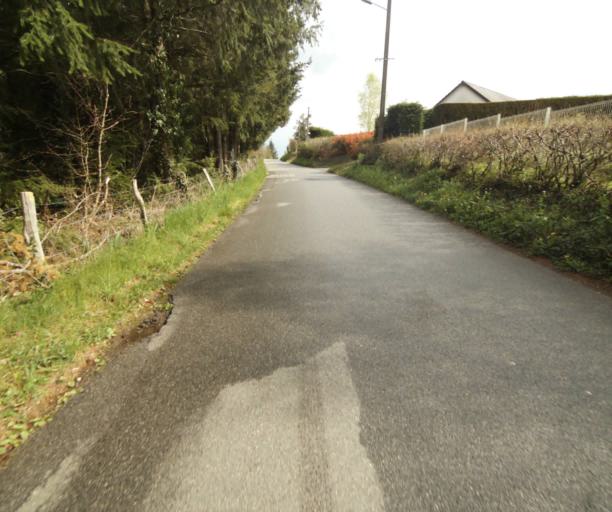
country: FR
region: Limousin
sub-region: Departement de la Correze
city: Tulle
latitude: 45.2763
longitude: 1.7507
